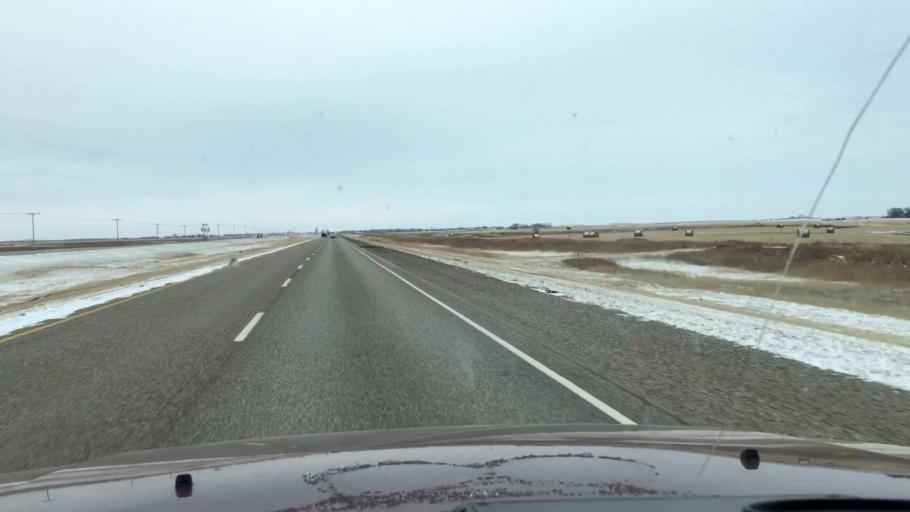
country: CA
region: Saskatchewan
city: Watrous
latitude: 51.0819
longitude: -105.8500
